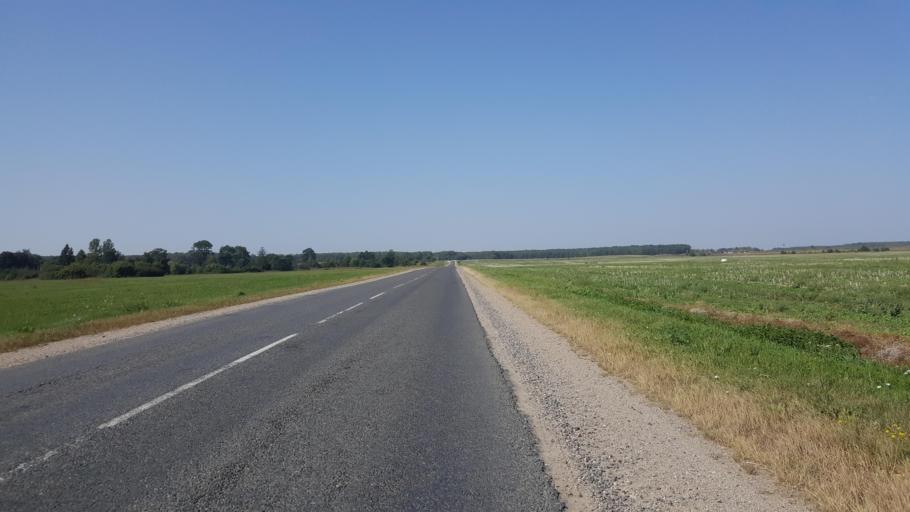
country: BY
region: Brest
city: Kamyanyets
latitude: 52.4125
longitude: 23.6006
